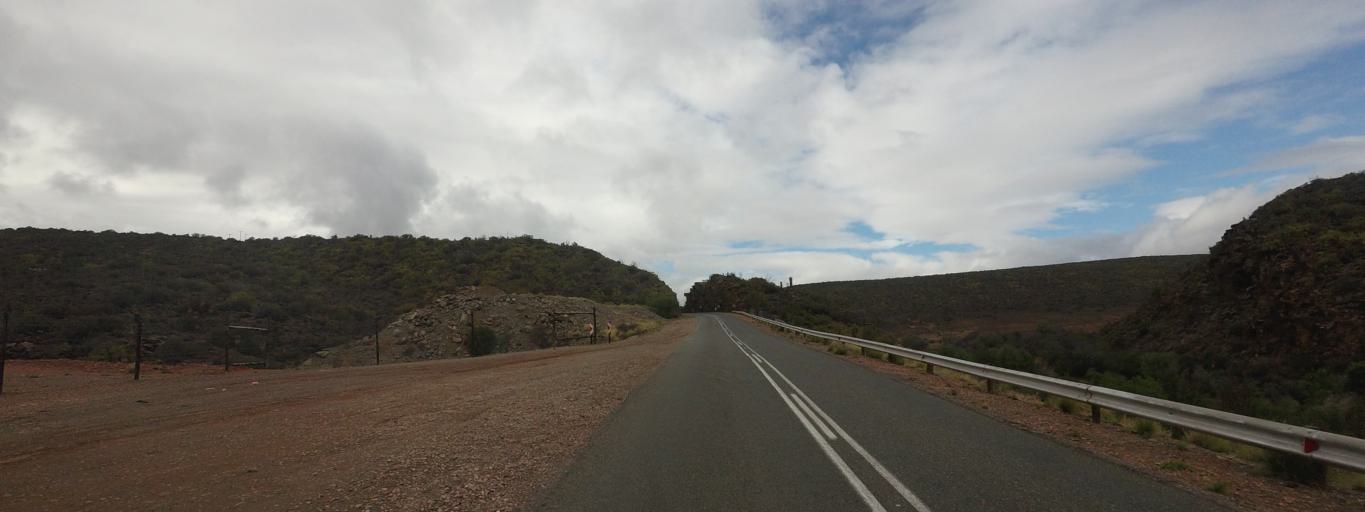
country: ZA
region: Western Cape
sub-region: Eden District Municipality
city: Oudtshoorn
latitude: -33.6799
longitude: 22.2494
